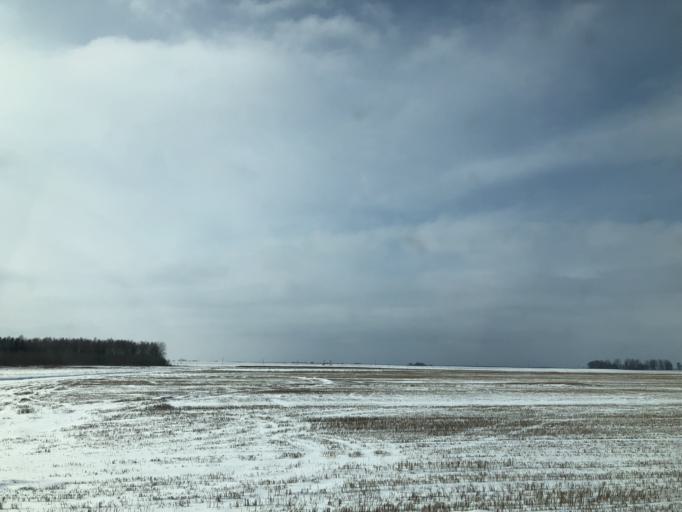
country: BY
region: Minsk
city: Kapyl'
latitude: 53.2815
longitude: 27.0804
